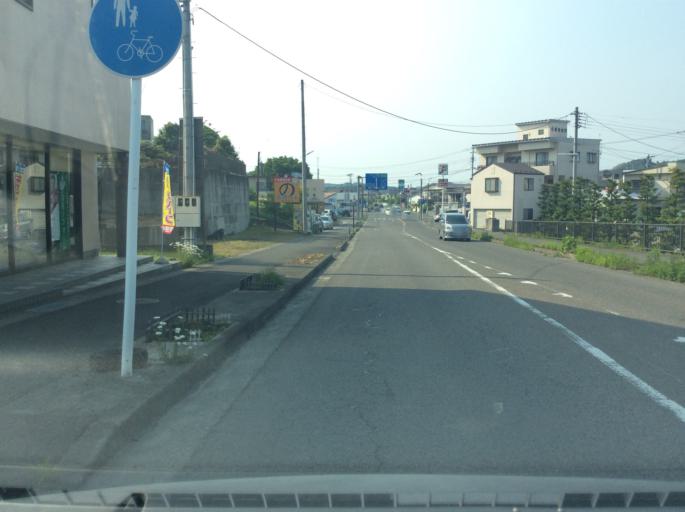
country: JP
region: Fukushima
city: Ishikawa
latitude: 37.1195
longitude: 140.2277
